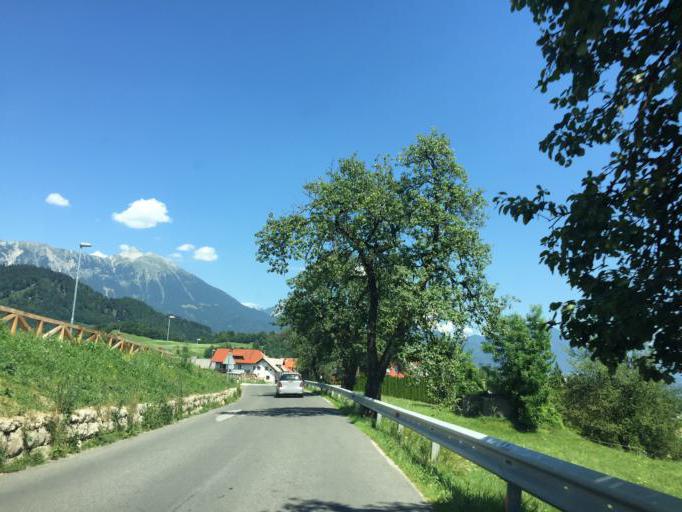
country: SI
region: Gorje
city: Zgornje Gorje
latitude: 46.3797
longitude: 14.0740
